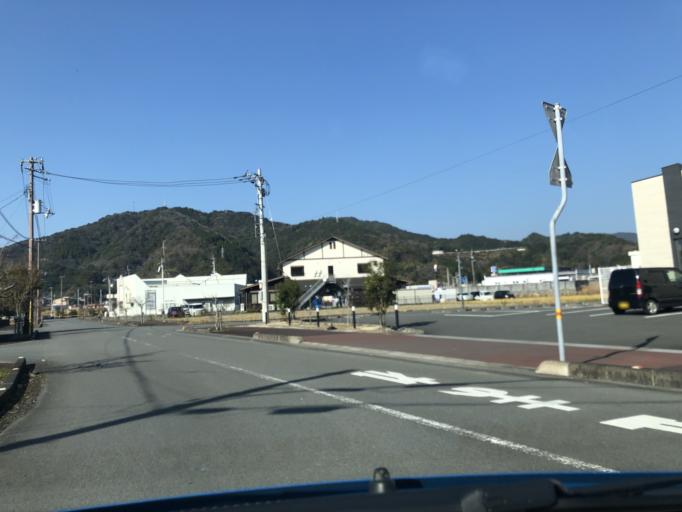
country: JP
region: Kochi
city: Sukumo
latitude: 32.9326
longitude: 132.7187
